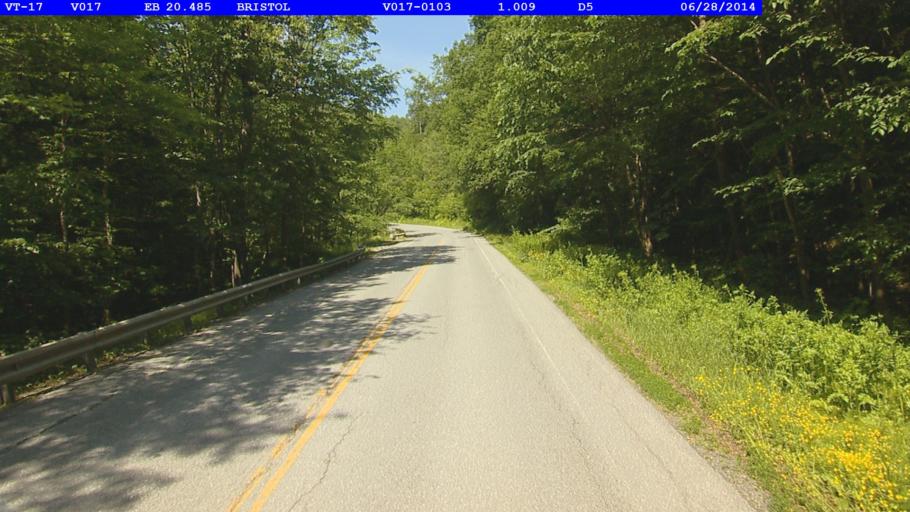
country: US
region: Vermont
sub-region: Addison County
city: Bristol
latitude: 44.1579
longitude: -73.0410
